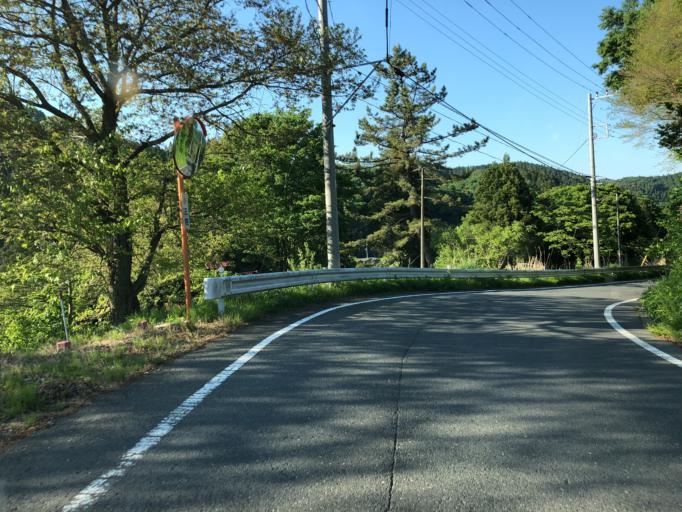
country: JP
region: Ibaraki
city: Kitaibaraki
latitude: 36.9152
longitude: 140.5811
